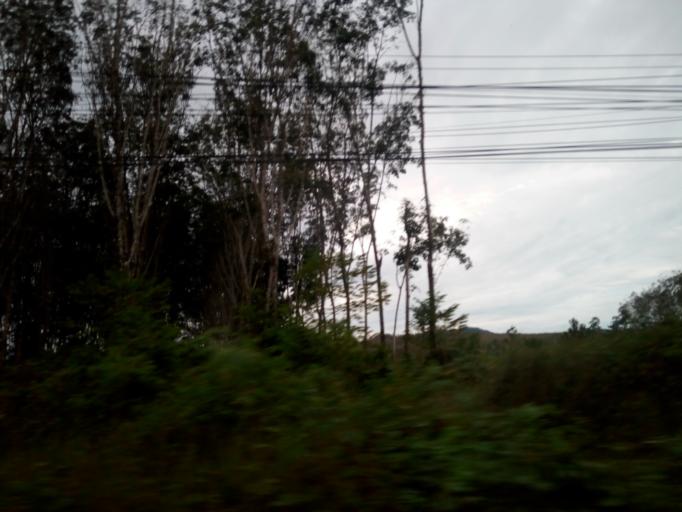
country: TH
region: Phuket
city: Thalang
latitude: 8.0596
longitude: 98.4019
